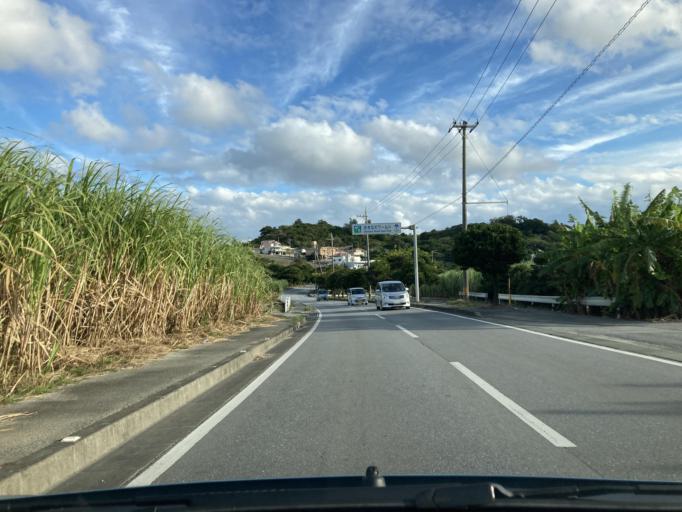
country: JP
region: Okinawa
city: Tomigusuku
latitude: 26.1517
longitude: 127.7434
